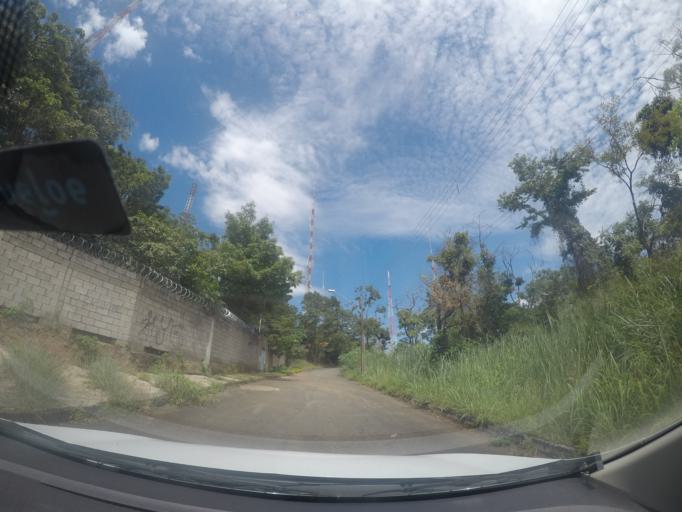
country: BR
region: Goias
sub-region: Goiania
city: Goiania
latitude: -16.6634
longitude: -49.3384
